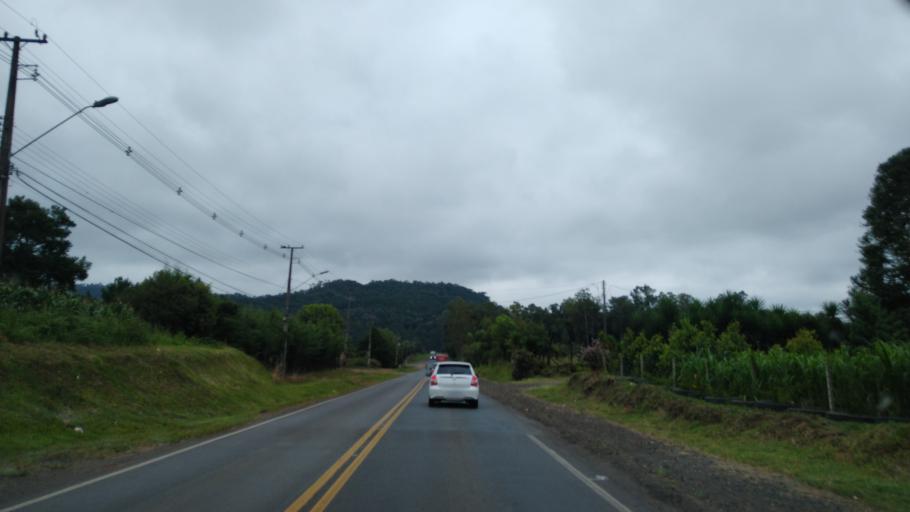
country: BR
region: Parana
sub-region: Uniao Da Vitoria
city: Uniao da Vitoria
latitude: -26.2373
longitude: -51.1251
